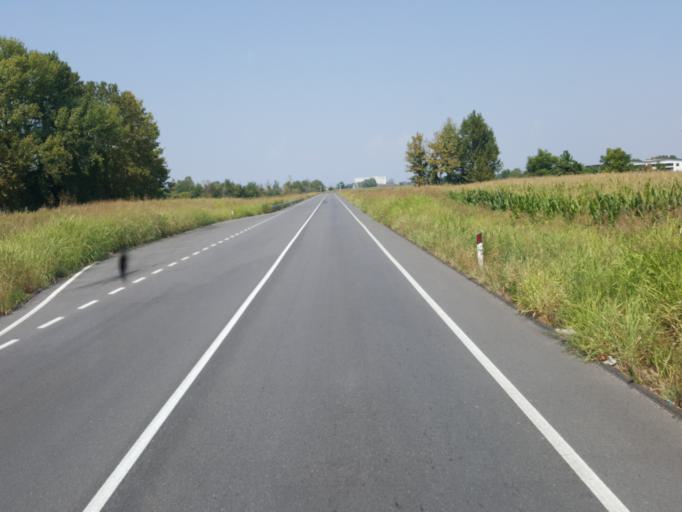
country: IT
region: Lombardy
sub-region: Provincia di Bergamo
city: Misano di Gera d'Adda
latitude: 45.4858
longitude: 9.6173
